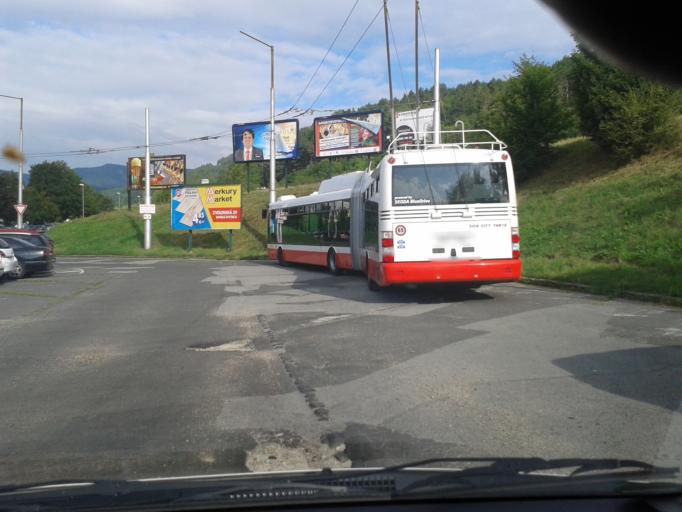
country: SK
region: Banskobystricky
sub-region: Okres Banska Bystrica
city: Banska Bystrica
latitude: 48.7450
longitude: 19.1170
